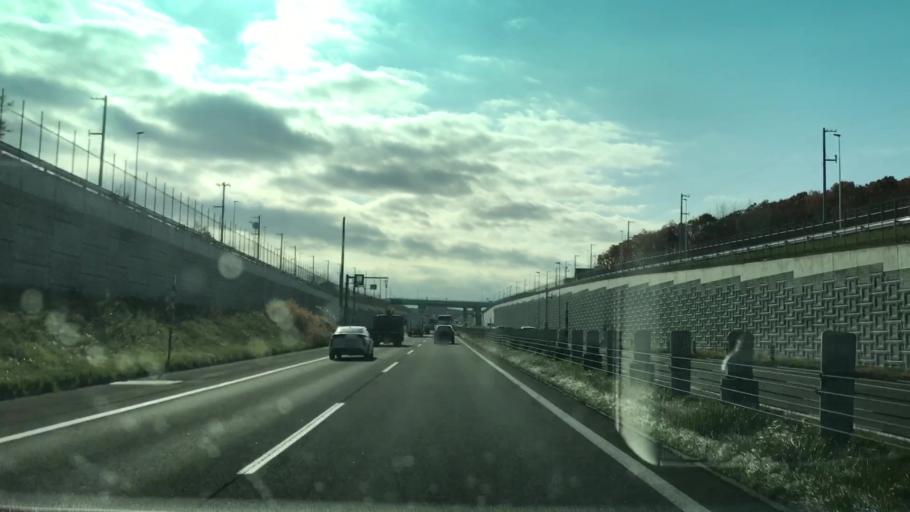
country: JP
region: Hokkaido
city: Kitahiroshima
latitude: 42.9972
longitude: 141.4686
